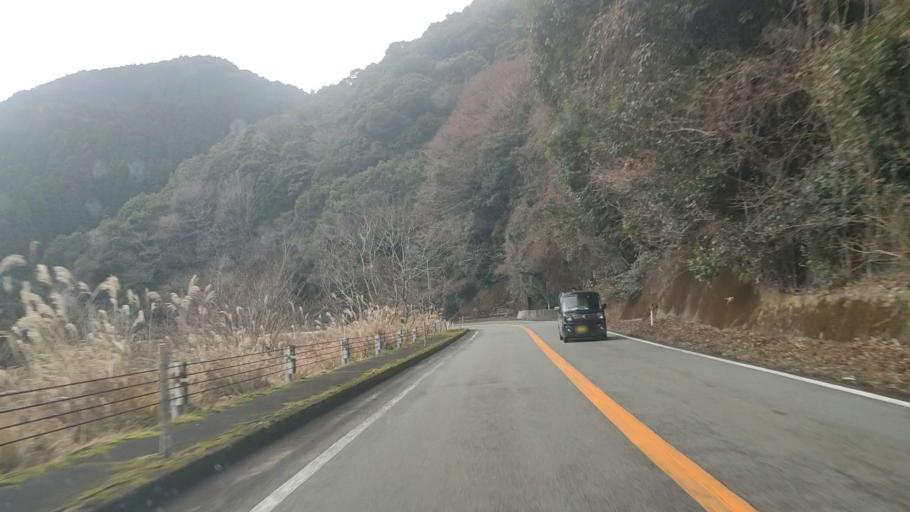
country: JP
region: Kumamoto
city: Hitoyoshi
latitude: 32.1220
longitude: 130.8084
